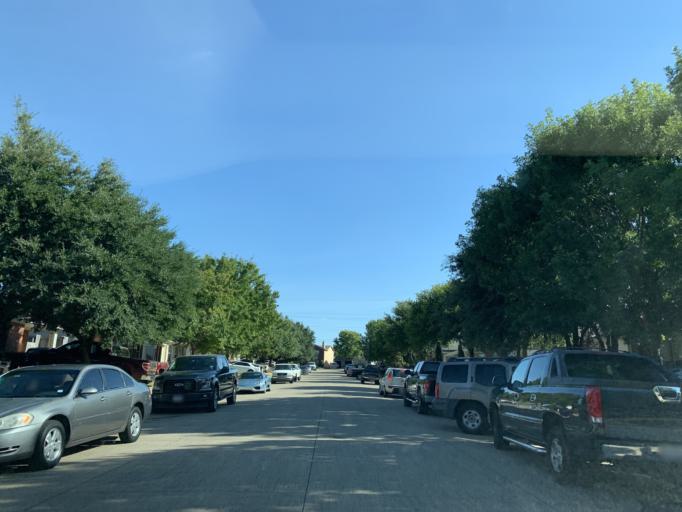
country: US
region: Texas
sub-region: Dallas County
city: Cockrell Hill
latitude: 32.7081
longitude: -96.8970
